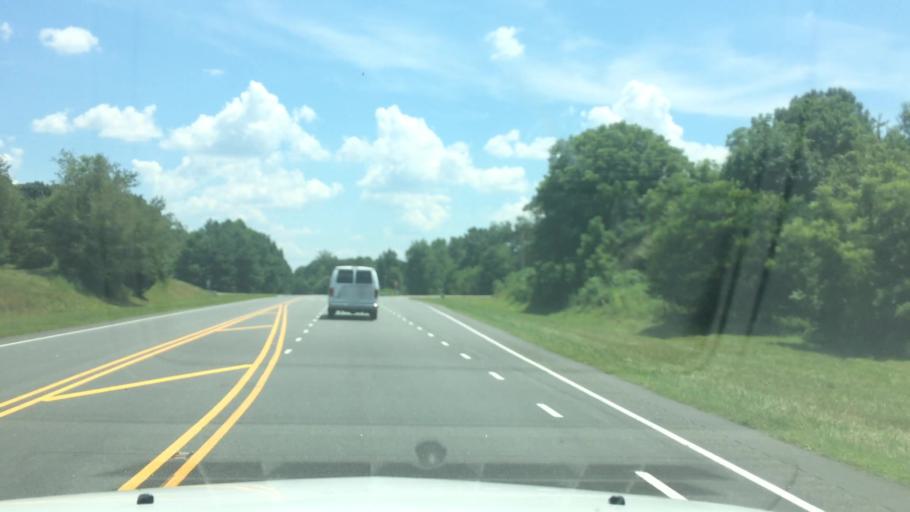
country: US
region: North Carolina
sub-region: Alexander County
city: Stony Point
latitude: 35.8183
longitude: -81.0025
